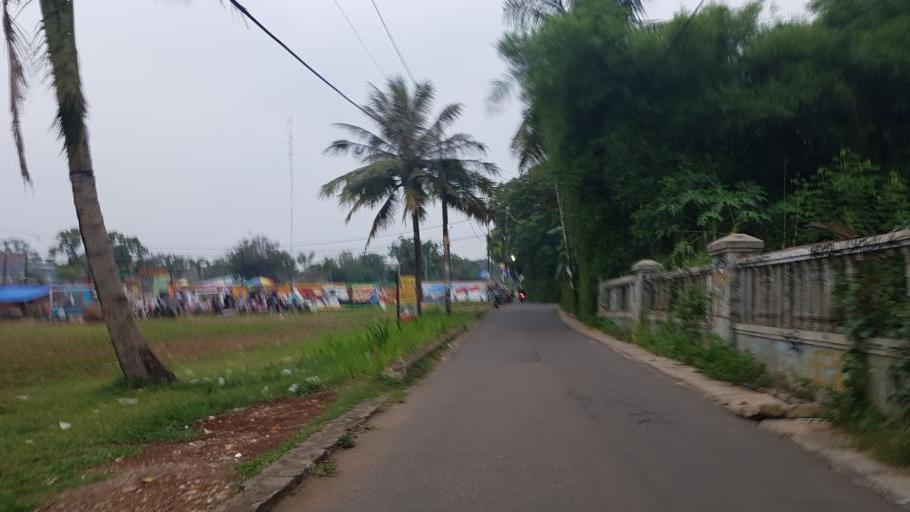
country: ID
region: West Java
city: Depok
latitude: -6.3703
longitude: 106.8020
